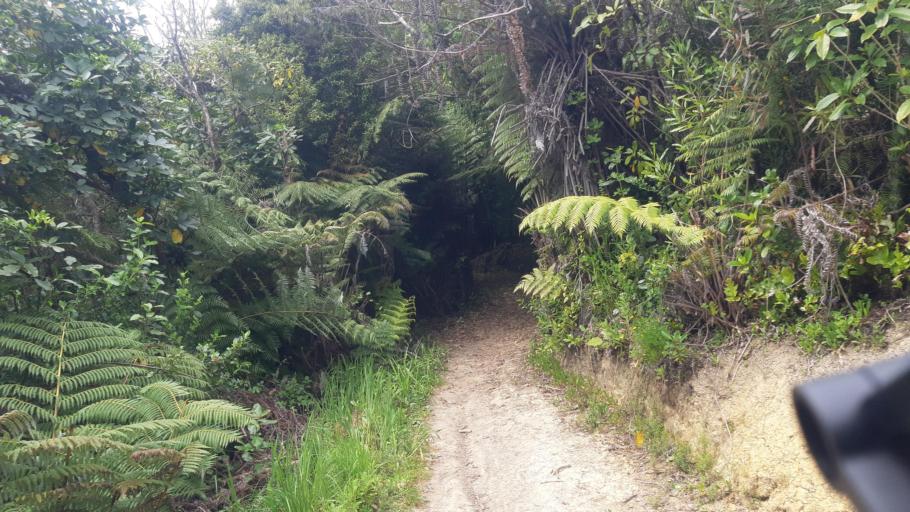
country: NZ
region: Marlborough
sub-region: Marlborough District
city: Picton
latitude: -41.2661
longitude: 173.9980
